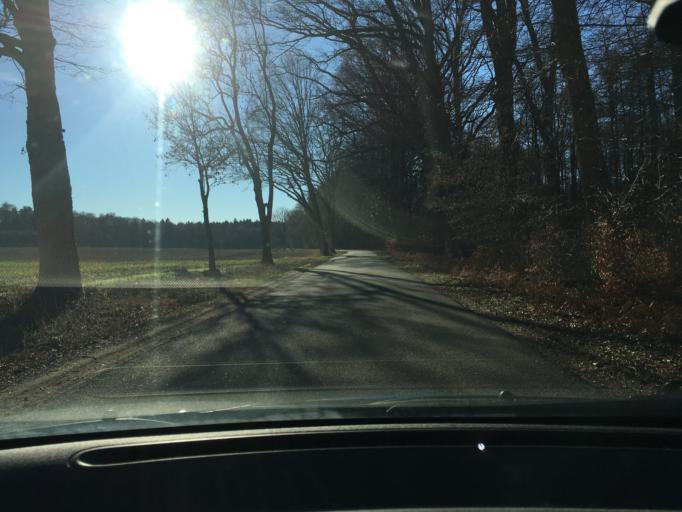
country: DE
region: Lower Saxony
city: Betzendorf
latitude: 53.1509
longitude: 10.3377
